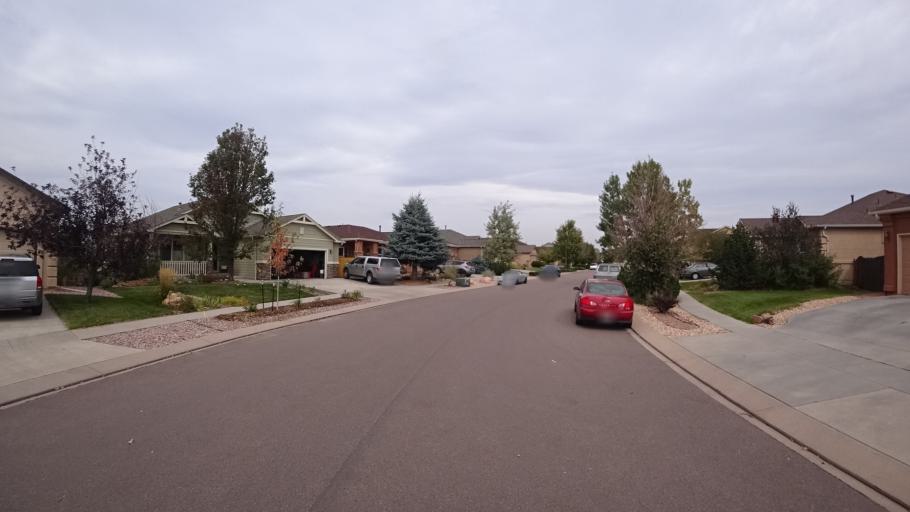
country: US
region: Colorado
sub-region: El Paso County
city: Cimarron Hills
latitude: 38.9188
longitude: -104.6914
